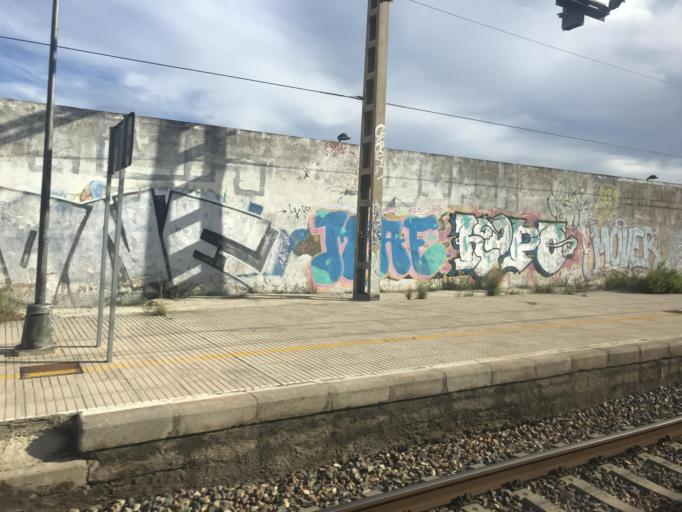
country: ES
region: Valencia
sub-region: Provincia de Castello
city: Benicarlo
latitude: 40.4292
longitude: 0.4165
